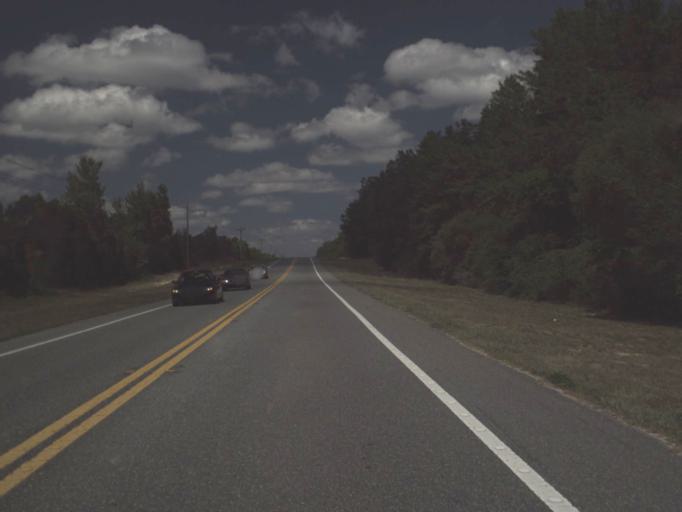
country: US
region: Florida
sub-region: Lake County
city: Astor
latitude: 29.1778
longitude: -81.7404
